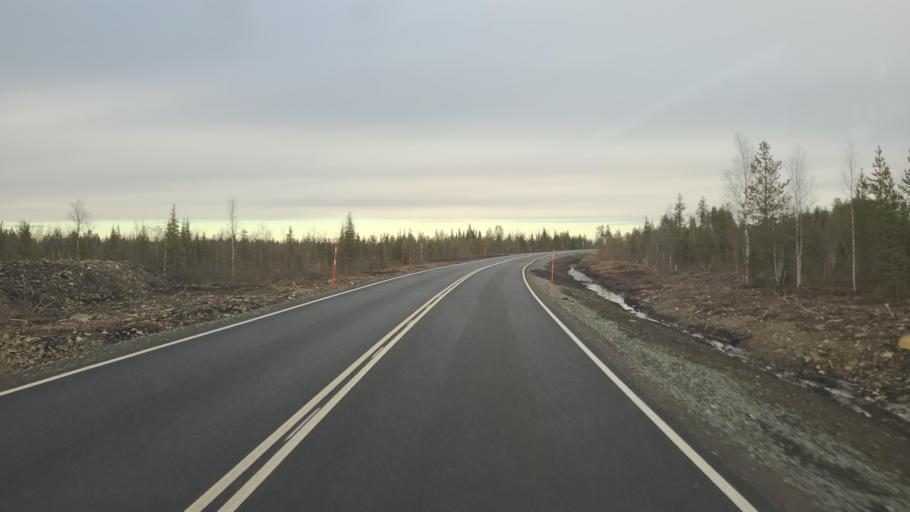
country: FI
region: Lapland
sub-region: Tunturi-Lappi
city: Kittilae
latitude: 67.8810
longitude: 25.0383
